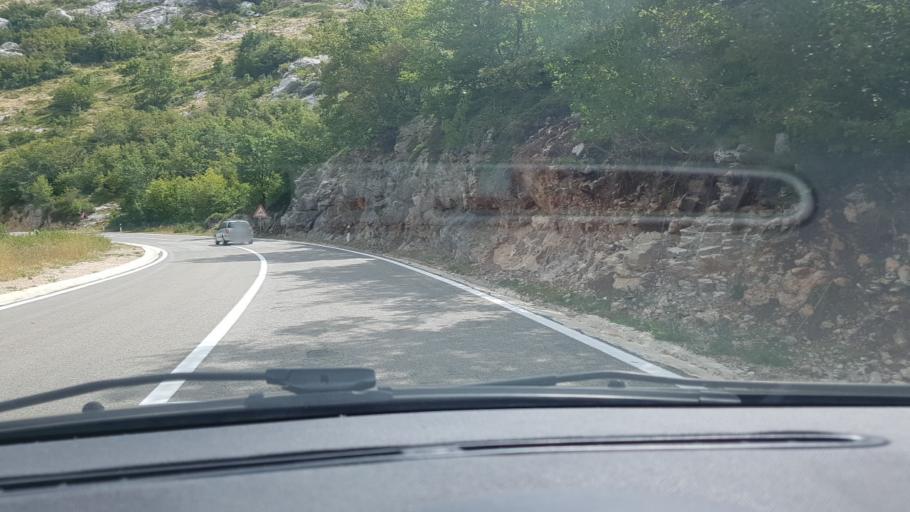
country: HR
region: Zadarska
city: Gracac
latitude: 44.2448
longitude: 15.8098
